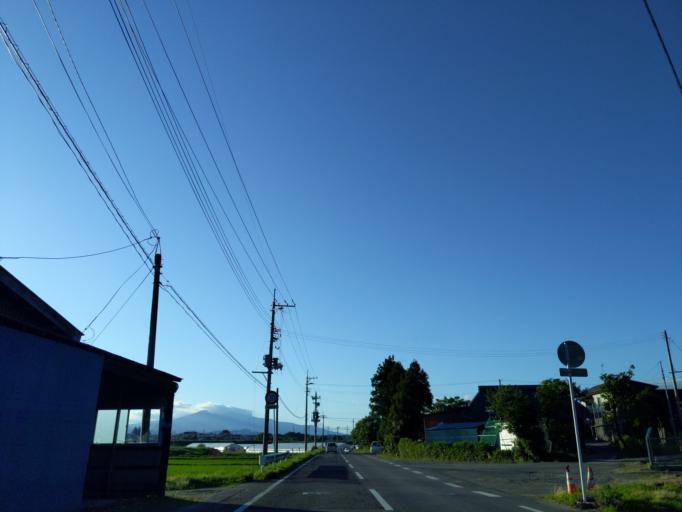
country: JP
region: Fukushima
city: Koriyama
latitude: 37.4102
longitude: 140.4128
